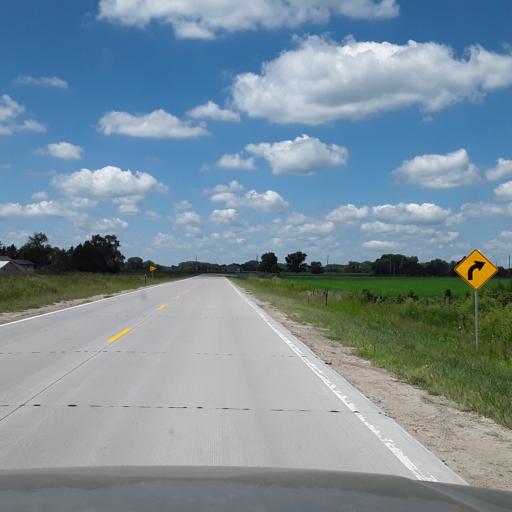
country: US
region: Nebraska
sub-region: Nance County
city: Genoa
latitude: 41.4262
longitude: -97.7310
